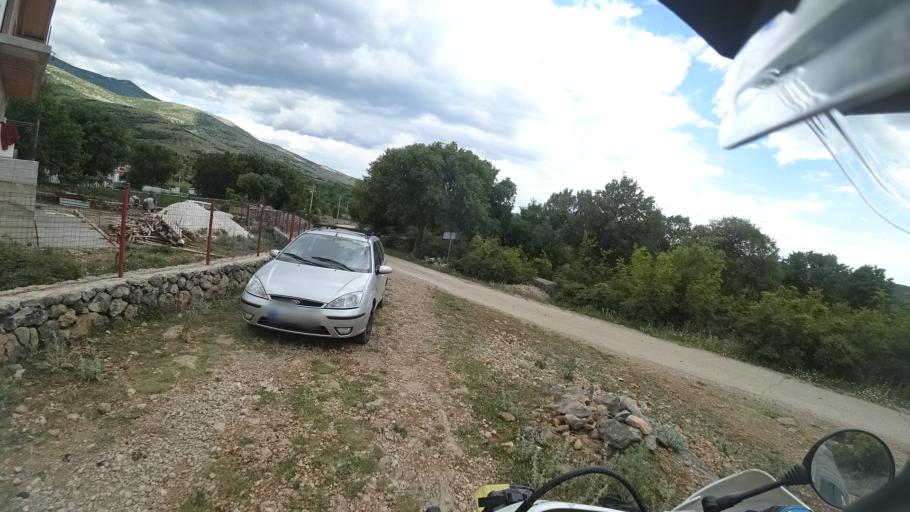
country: HR
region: Zadarska
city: Gracac
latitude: 44.1944
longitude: 15.9073
